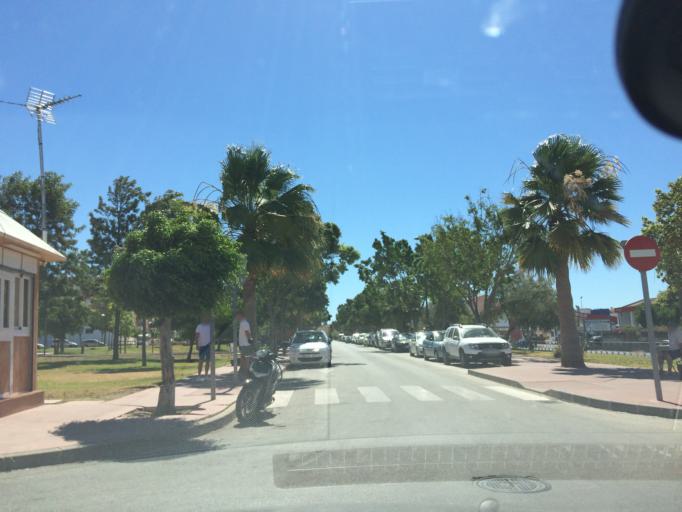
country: ES
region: Andalusia
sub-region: Provincia de Malaga
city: Estacion de Cartama
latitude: 36.7372
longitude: -4.6078
